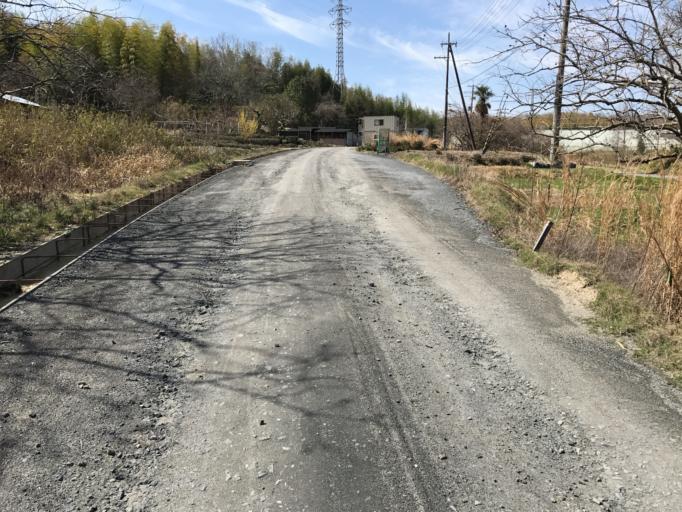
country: JP
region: Kyoto
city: Tanabe
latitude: 34.7836
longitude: 135.7800
